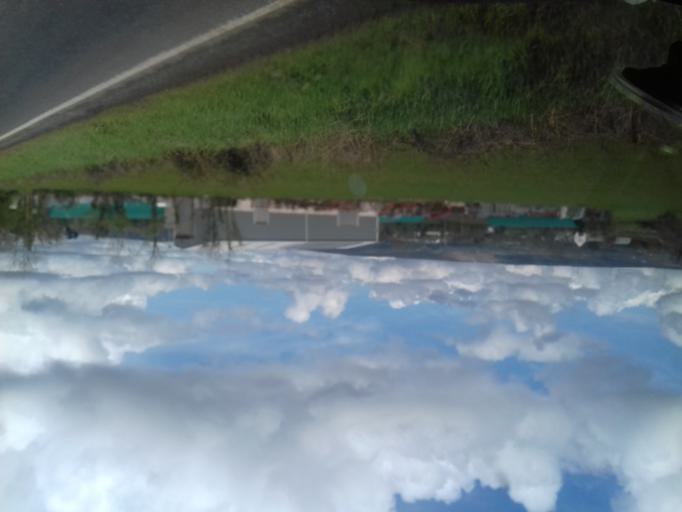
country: IE
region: Ulster
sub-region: An Cabhan
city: Ballyconnell
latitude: 54.1481
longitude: -7.5196
